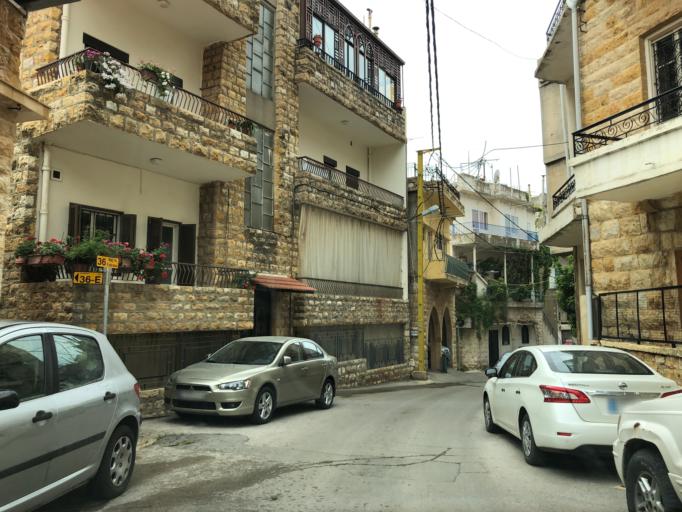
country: LB
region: Mont-Liban
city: Jdaidet el Matn
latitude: 33.8821
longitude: 35.6286
